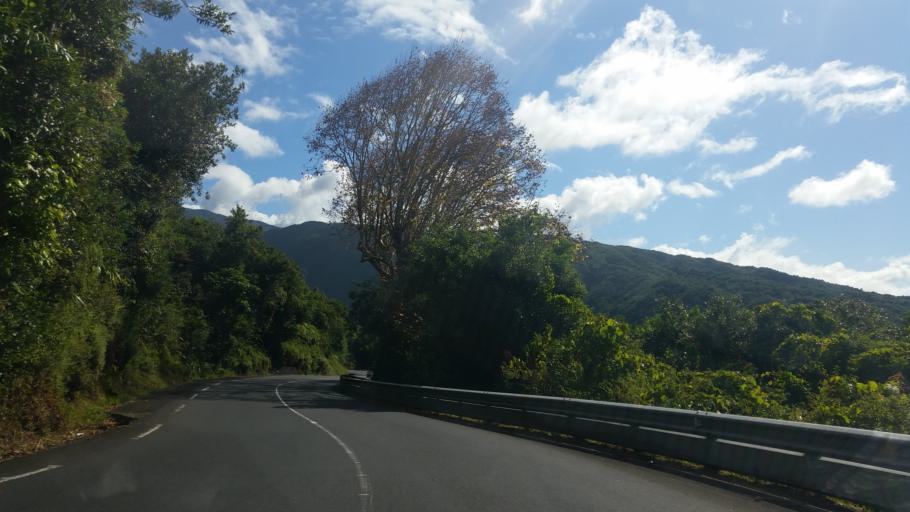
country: RE
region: Reunion
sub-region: Reunion
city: Saint-Benoit
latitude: -21.1026
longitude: 55.6723
